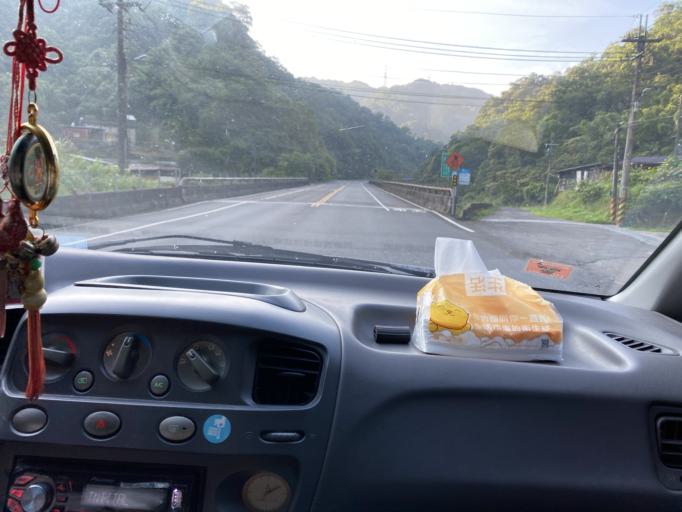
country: TW
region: Taiwan
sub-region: Keelung
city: Keelung
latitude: 25.0306
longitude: 121.7792
